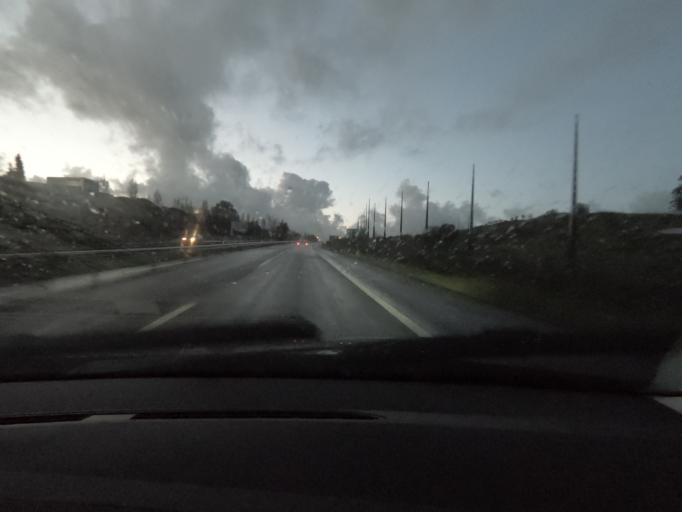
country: PT
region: Lisbon
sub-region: Sintra
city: Cacem
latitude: 38.7436
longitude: -9.3015
